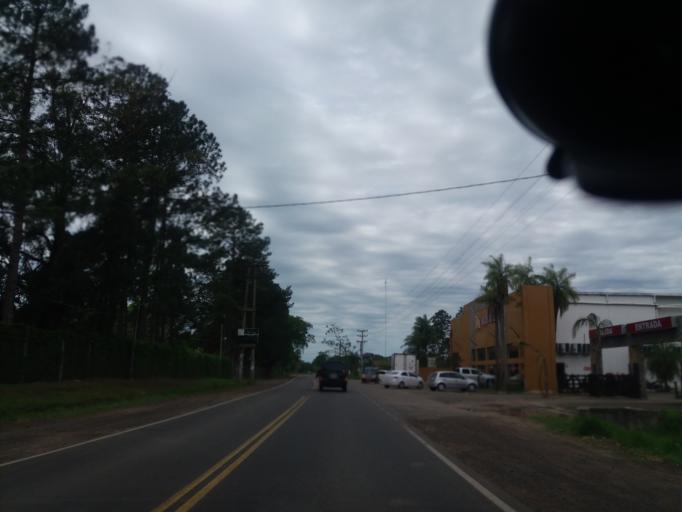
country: AR
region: Corrientes
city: Corrientes
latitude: -27.4512
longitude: -58.7337
